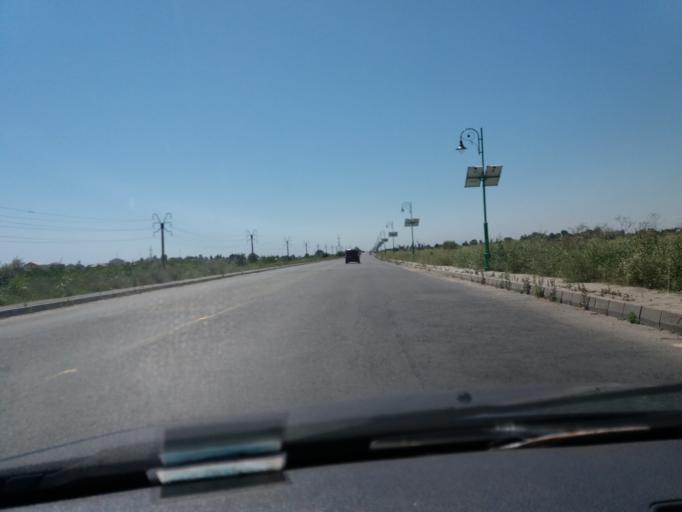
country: RO
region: Constanta
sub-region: Comuna Navodari
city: Navodari
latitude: 44.3079
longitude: 28.6155
